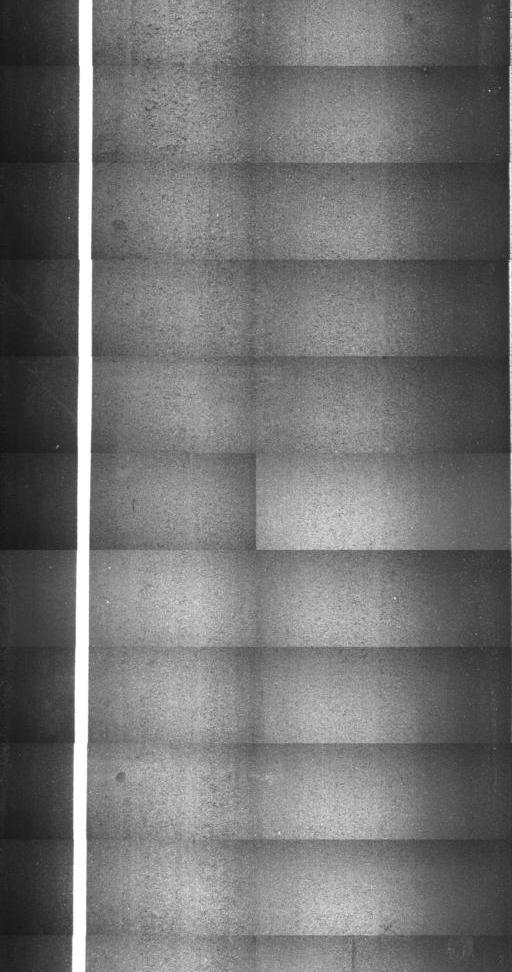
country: US
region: Vermont
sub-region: Windsor County
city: Windsor
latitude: 43.4843
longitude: -72.3853
